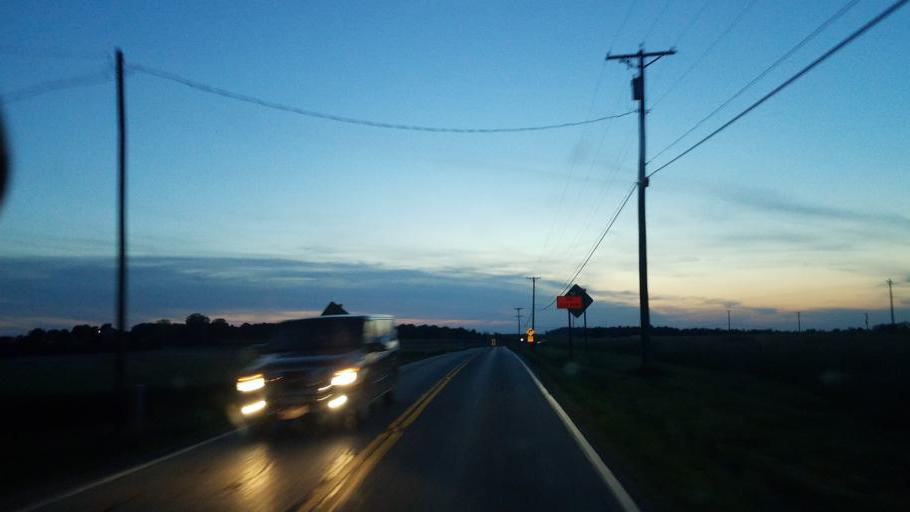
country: US
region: Ohio
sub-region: Highland County
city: Greenfield
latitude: 39.2439
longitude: -83.4362
